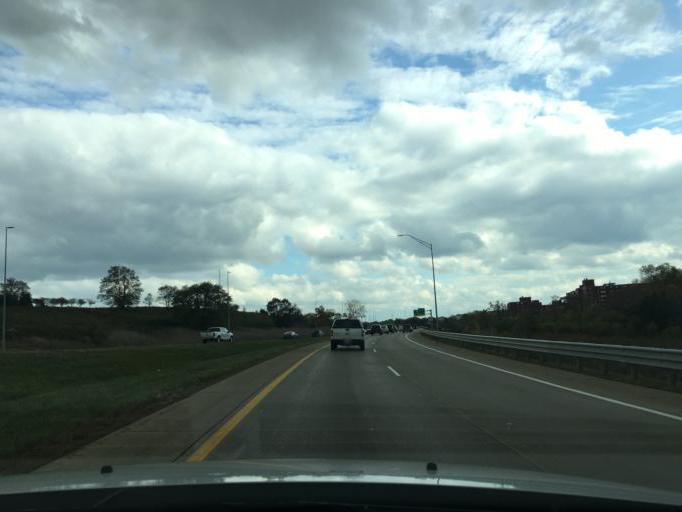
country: US
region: Michigan
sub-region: Oakland County
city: Bingham Farms
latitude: 42.4932
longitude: -83.2946
